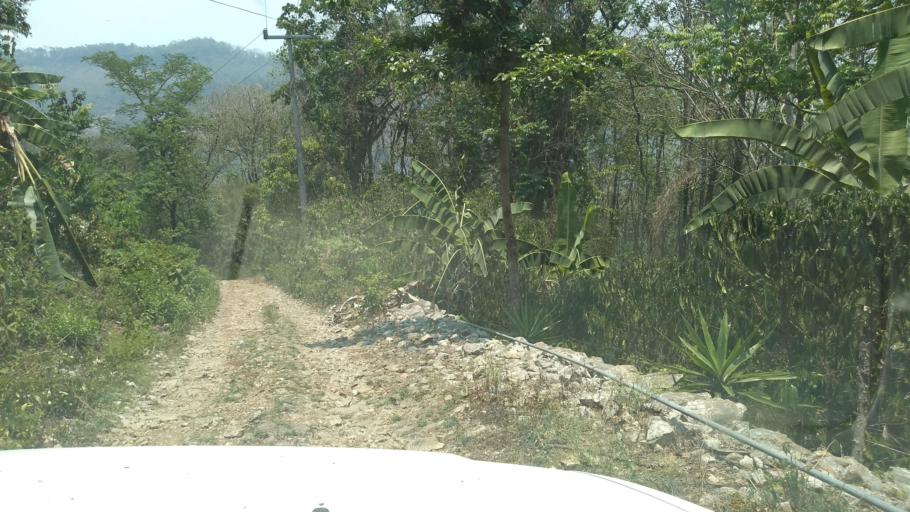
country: MX
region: Veracruz
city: Cosolapa
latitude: 18.5957
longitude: -96.7307
